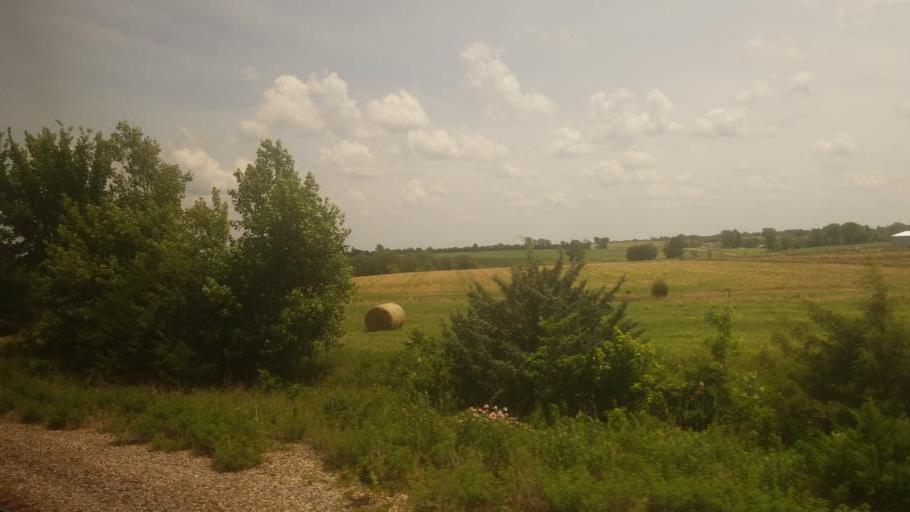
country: US
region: Missouri
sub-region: Macon County
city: La Plata
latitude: 40.0973
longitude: -92.4137
